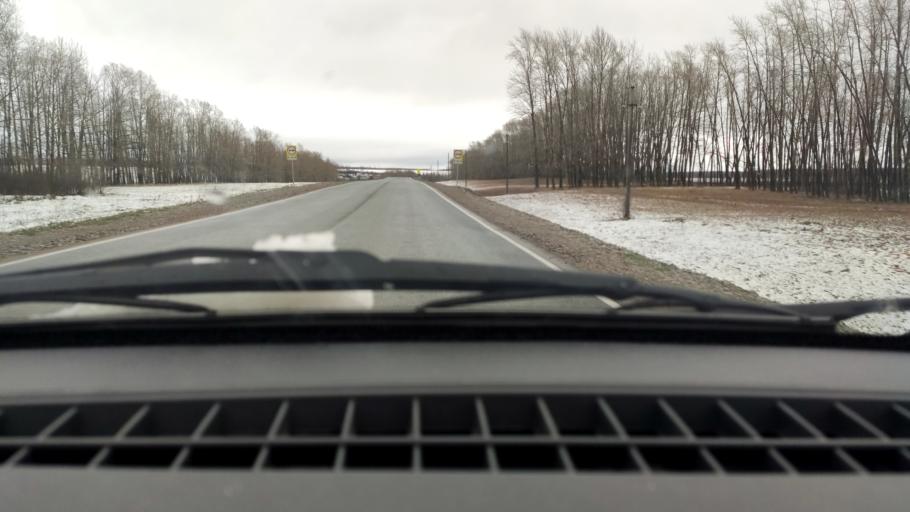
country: RU
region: Bashkortostan
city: Alekseyevka
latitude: 55.0591
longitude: 55.1103
